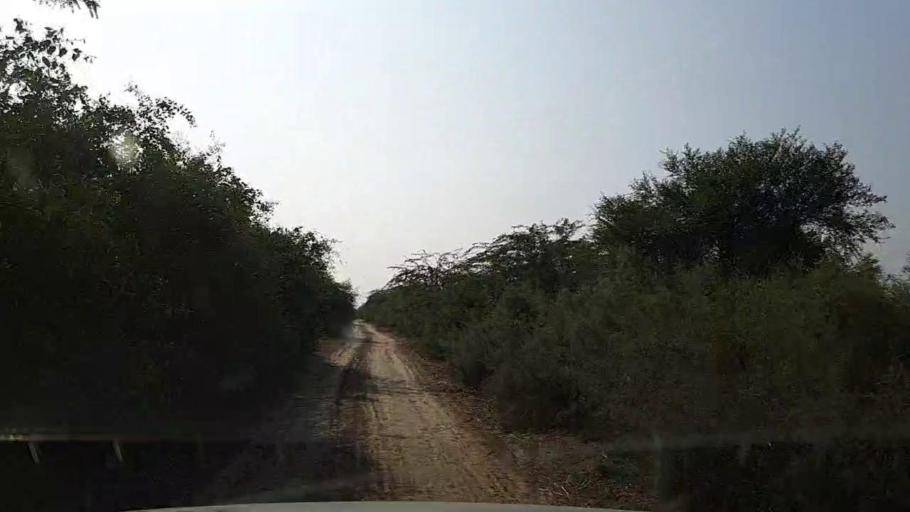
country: PK
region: Sindh
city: Mirpur Sakro
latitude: 24.5737
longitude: 67.5736
